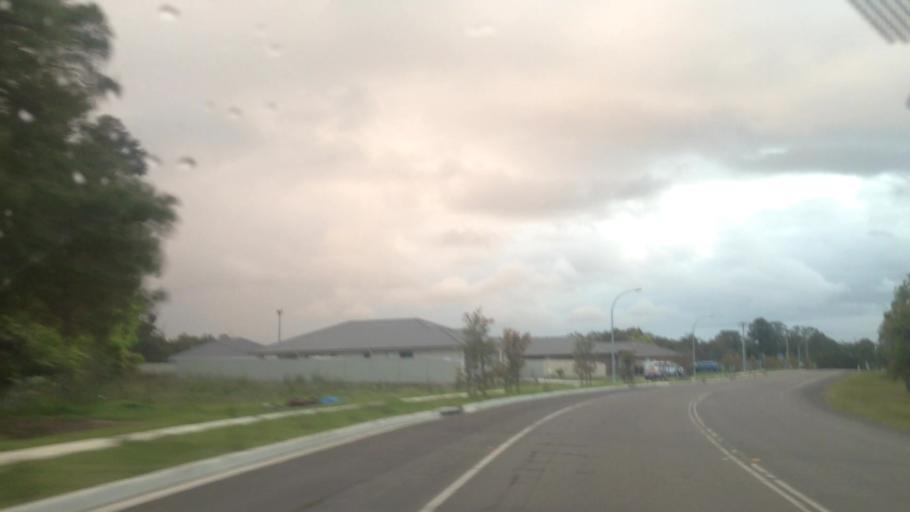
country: AU
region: New South Wales
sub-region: Lake Macquarie Shire
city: Dora Creek
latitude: -33.1036
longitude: 151.4773
